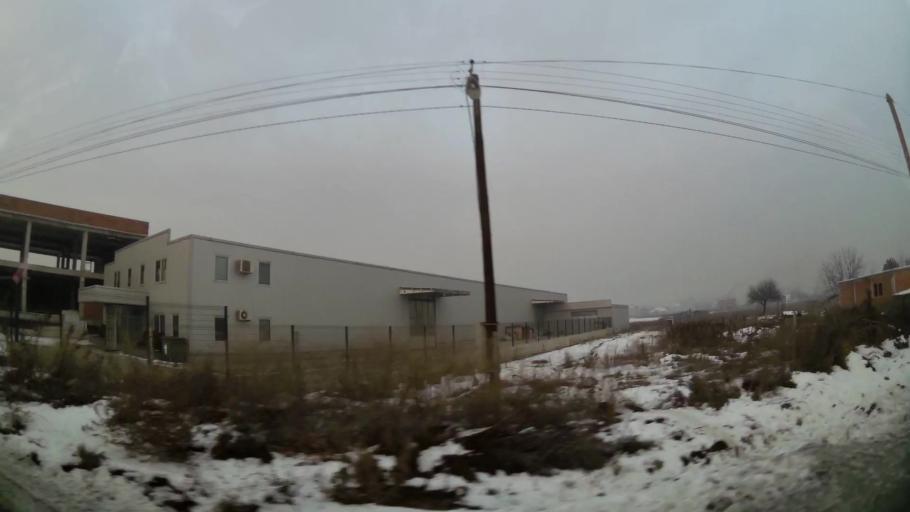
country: MK
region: Suto Orizari
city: Suto Orizare
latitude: 42.0364
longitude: 21.3999
